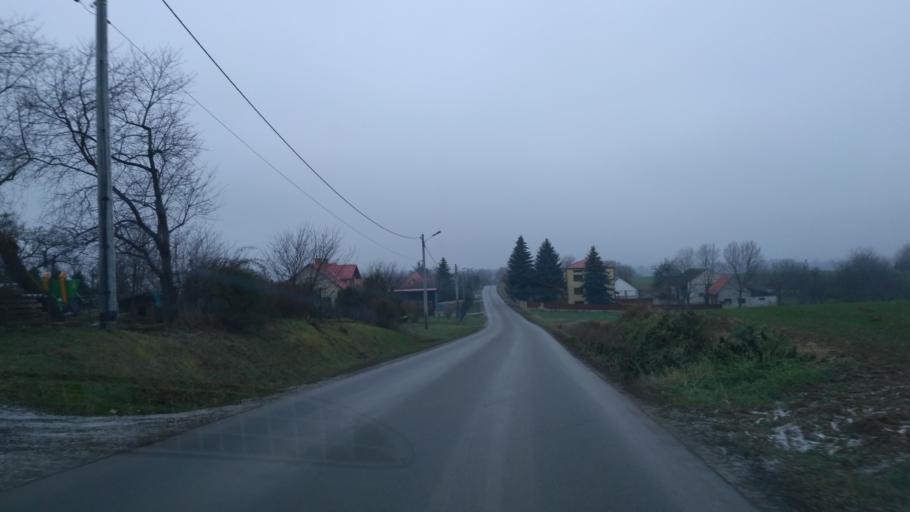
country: PL
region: Subcarpathian Voivodeship
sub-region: Powiat przeworski
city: Zurawiczki
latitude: 50.0028
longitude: 22.4886
